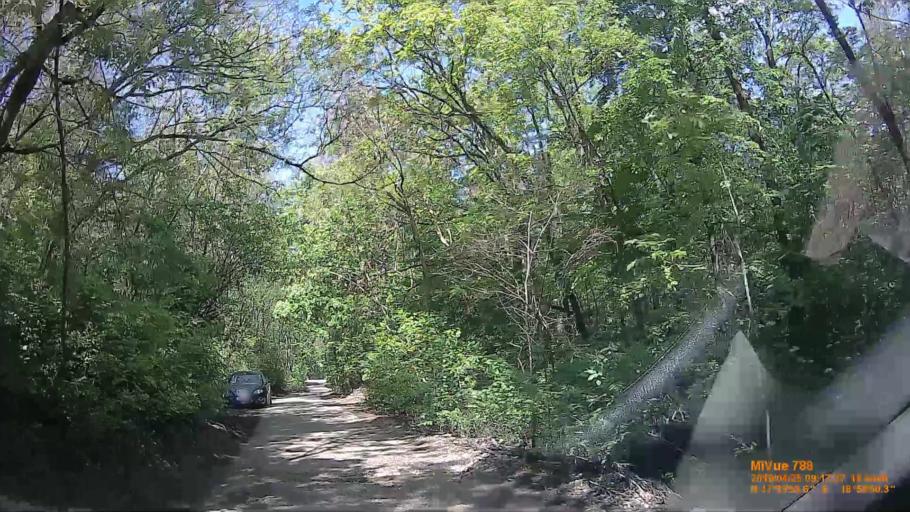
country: HU
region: Pest
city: Urom
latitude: 47.5649
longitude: 18.9973
